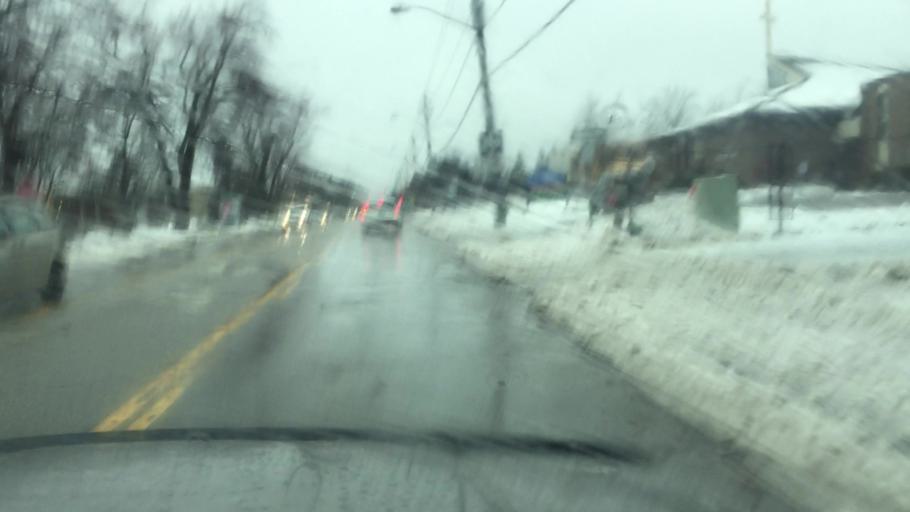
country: CA
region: Ontario
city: Ajax
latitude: 43.8561
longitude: -79.0563
